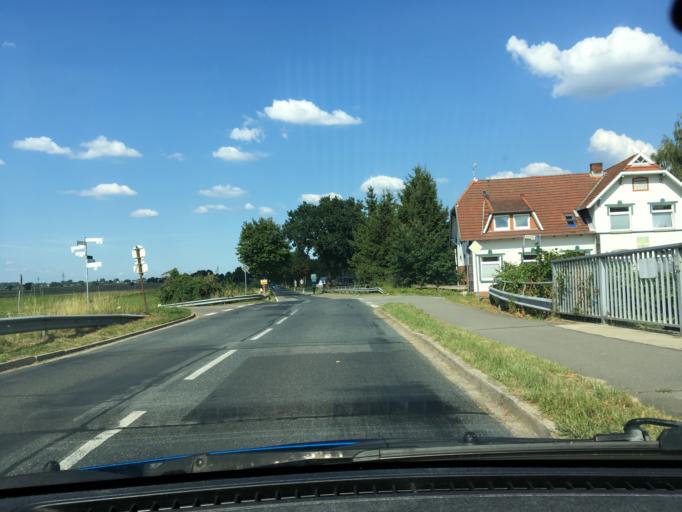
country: DE
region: Lower Saxony
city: Stelle
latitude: 53.3876
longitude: 10.1139
